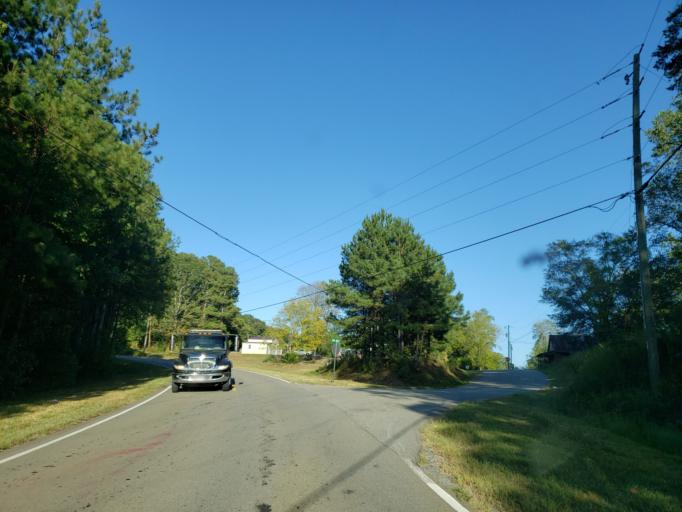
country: US
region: Georgia
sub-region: Pickens County
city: Nelson
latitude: 34.3911
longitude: -84.4045
